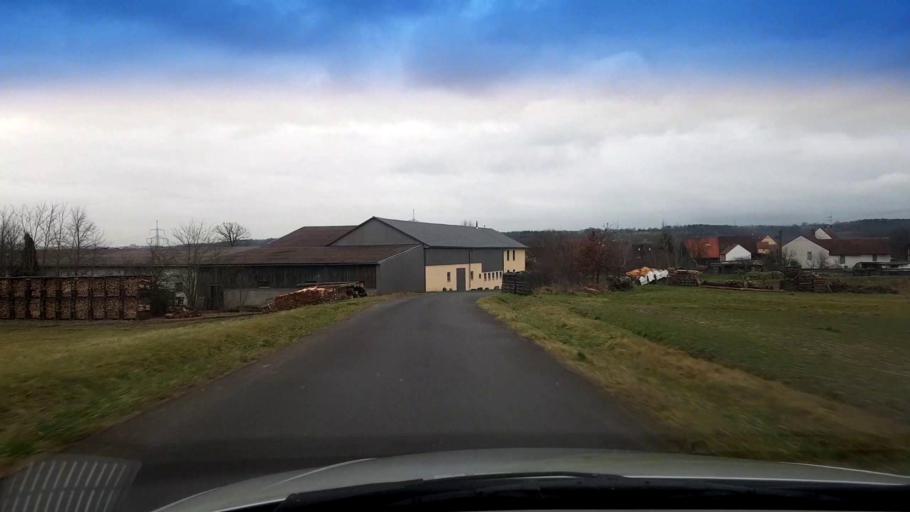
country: DE
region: Bavaria
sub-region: Upper Franconia
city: Viereth-Trunstadt
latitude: 49.9386
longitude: 10.7880
